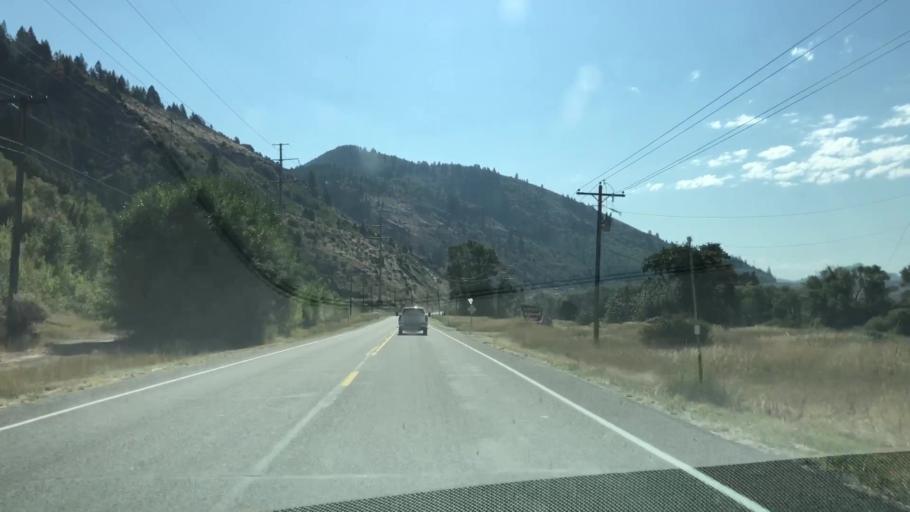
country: US
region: Idaho
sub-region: Teton County
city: Victor
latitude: 43.3482
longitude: -111.2128
